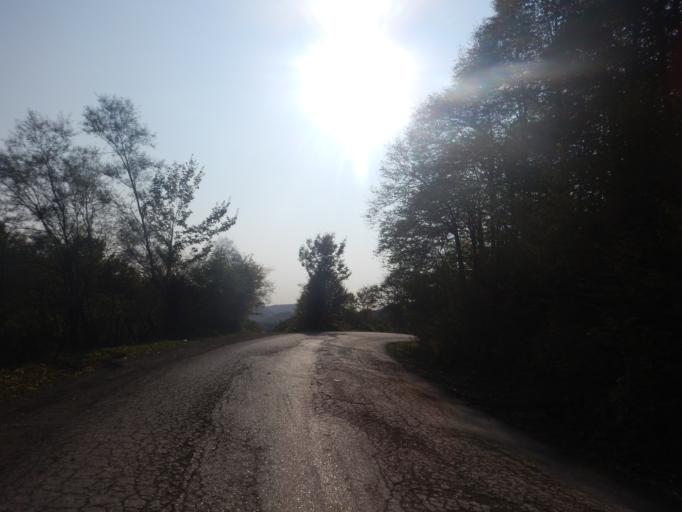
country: TR
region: Ordu
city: Golkoy
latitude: 40.6701
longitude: 37.5659
